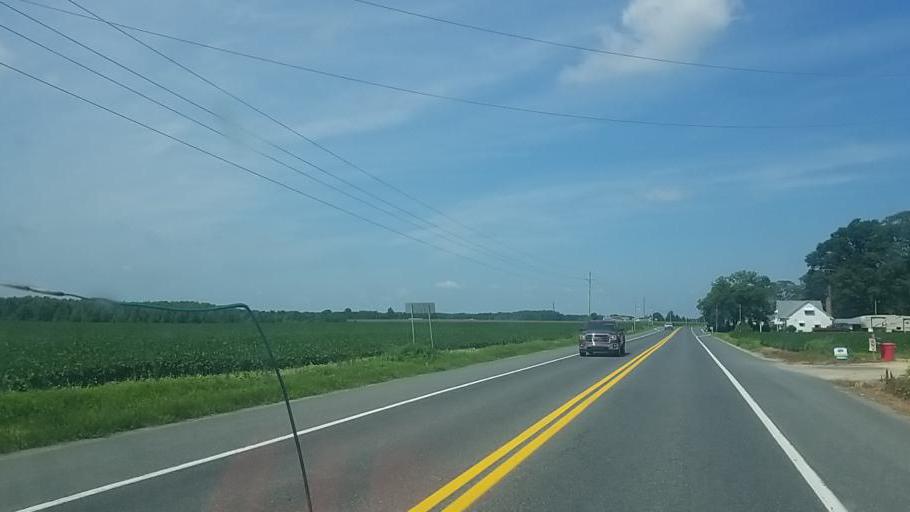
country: US
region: Delaware
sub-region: Sussex County
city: Bridgeville
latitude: 38.8257
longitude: -75.6503
